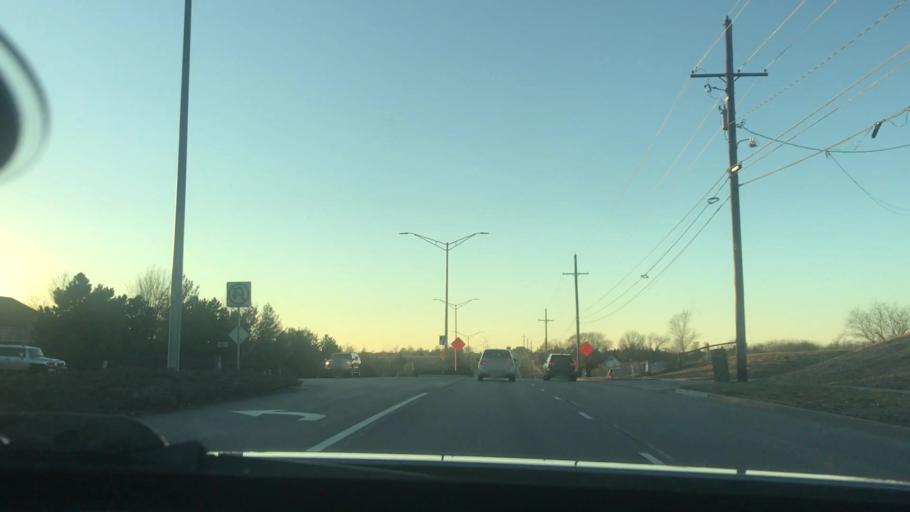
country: US
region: Kansas
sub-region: Johnson County
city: Olathe
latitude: 38.9274
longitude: -94.8447
